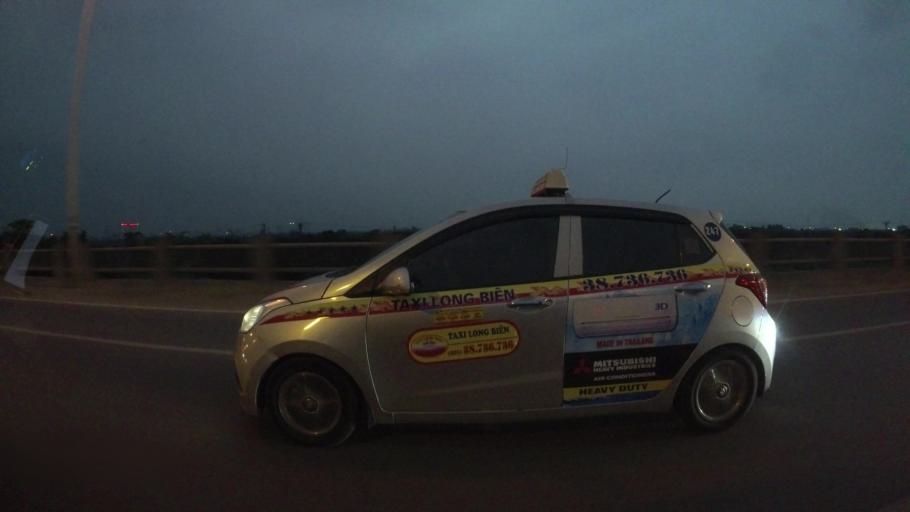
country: VN
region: Ha Noi
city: Hoan Kiem
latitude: 21.0167
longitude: 105.8888
